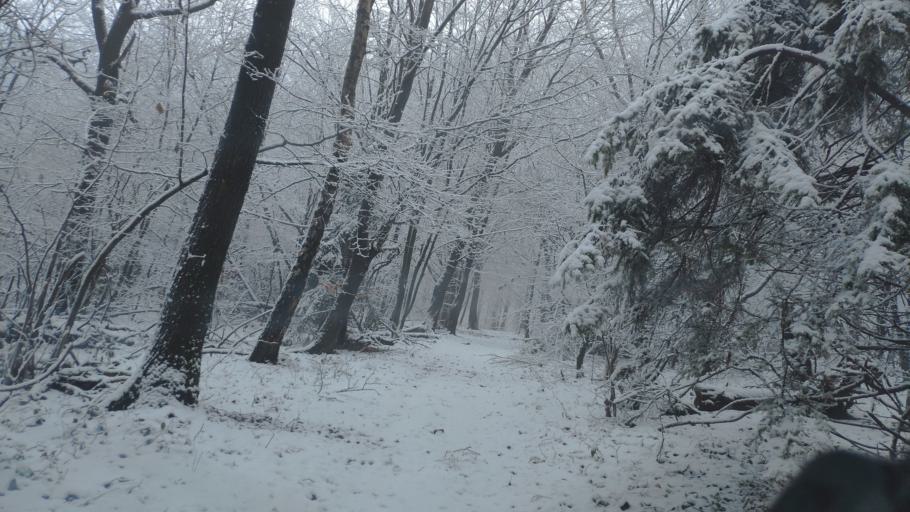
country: SK
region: Kosicky
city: Moldava nad Bodvou
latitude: 48.7390
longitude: 21.0940
